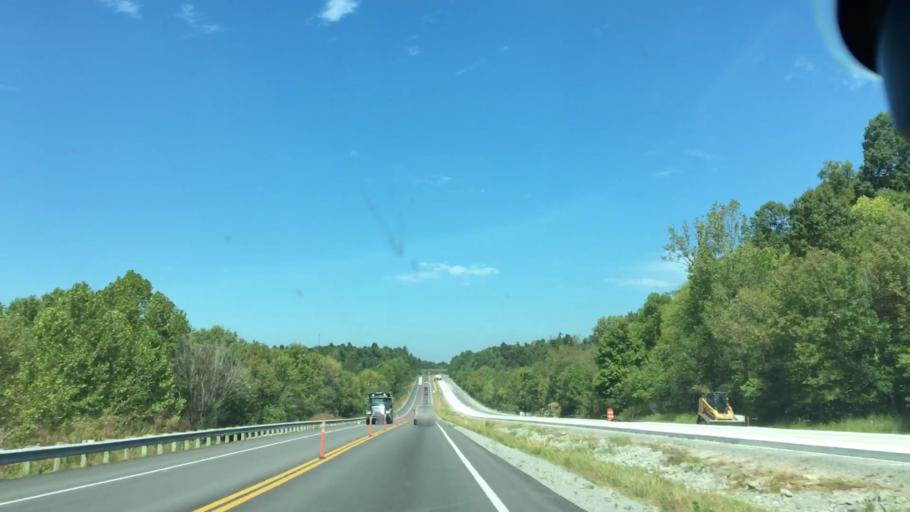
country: US
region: Kentucky
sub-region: Christian County
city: Hopkinsville
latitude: 36.9801
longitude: -87.4655
